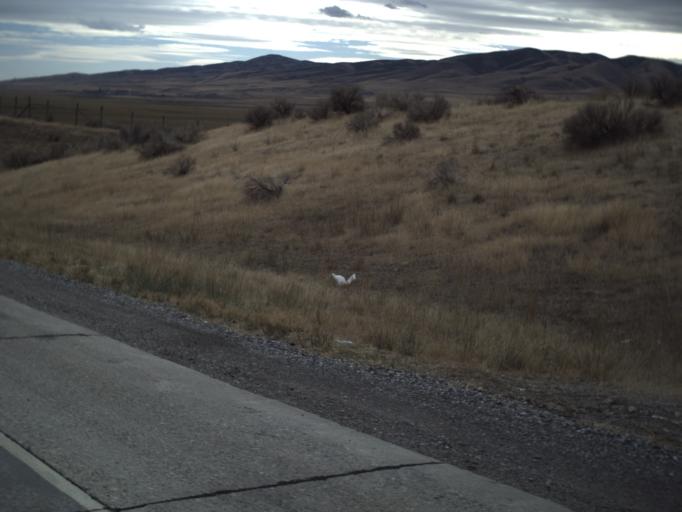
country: US
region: Idaho
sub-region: Oneida County
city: Malad City
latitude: 41.9777
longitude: -112.1912
